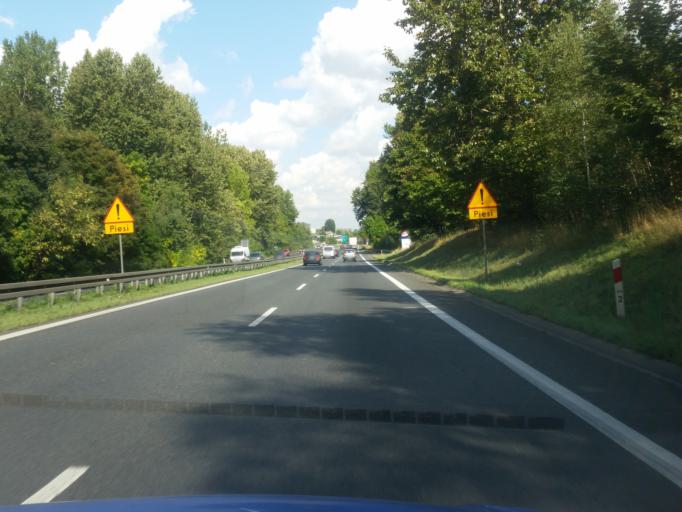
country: PL
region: Silesian Voivodeship
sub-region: Powiat bedzinski
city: Siewierz
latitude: 50.4477
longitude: 19.2248
